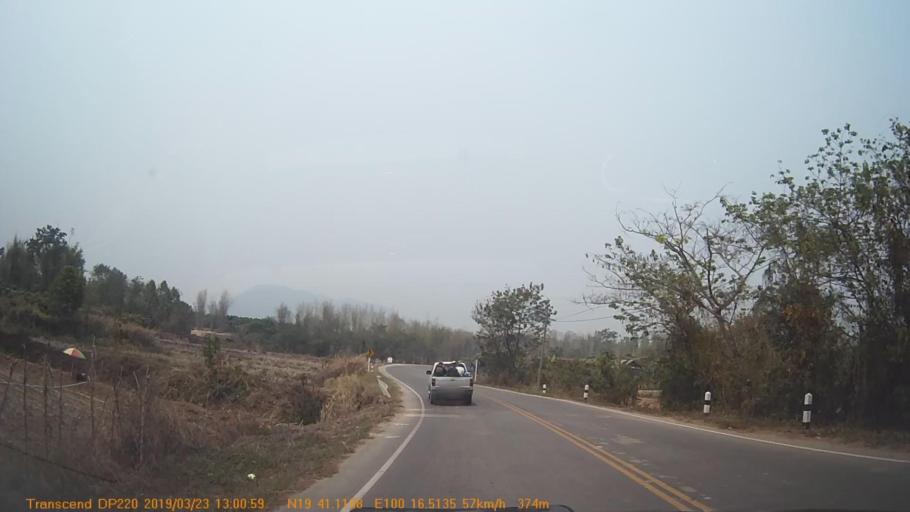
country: TH
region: Chiang Rai
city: Thoeng
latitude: 19.6854
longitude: 100.2752
